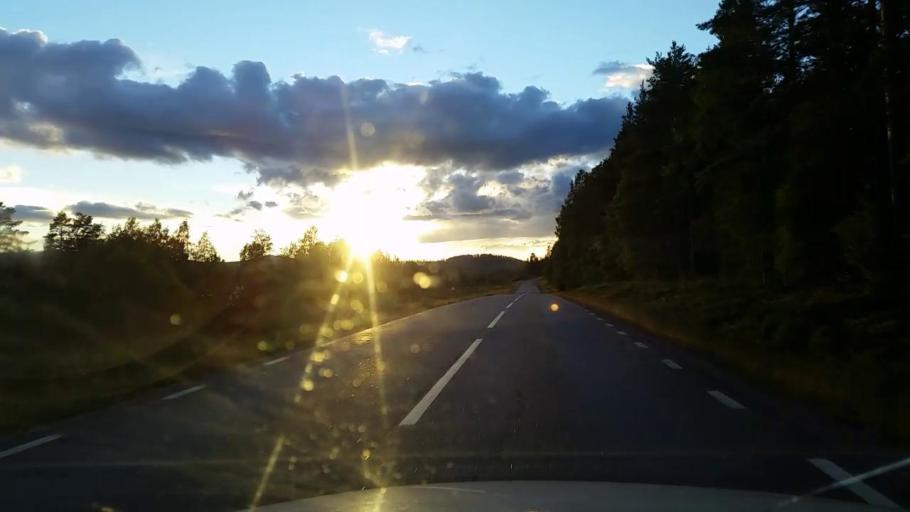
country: SE
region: Gaevleborg
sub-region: Ljusdals Kommun
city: Farila
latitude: 62.1339
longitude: 15.6952
